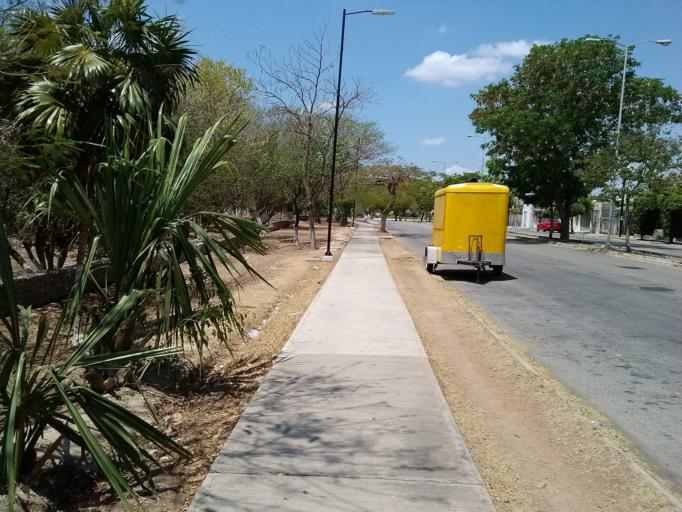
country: MX
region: Yucatan
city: Merida
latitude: 20.9698
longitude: -89.5840
